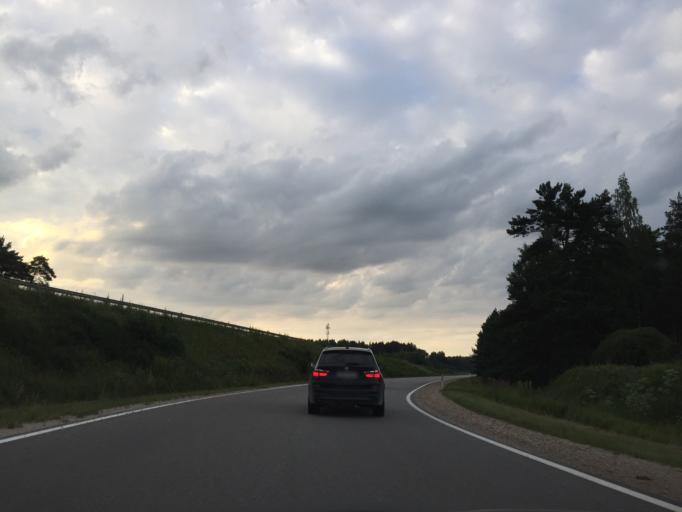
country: LV
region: Babite
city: Pinki
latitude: 56.9233
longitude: 23.9150
